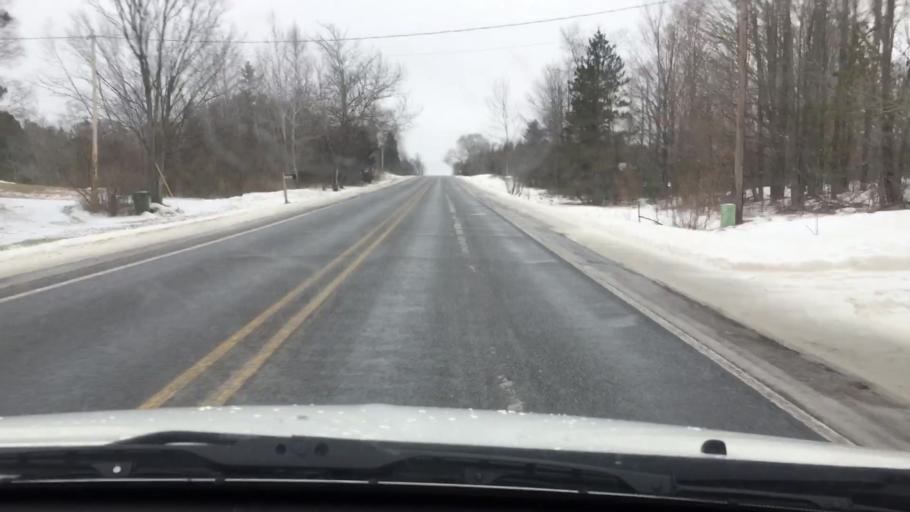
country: US
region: Michigan
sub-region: Wexford County
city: Cadillac
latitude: 44.0948
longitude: -85.4442
